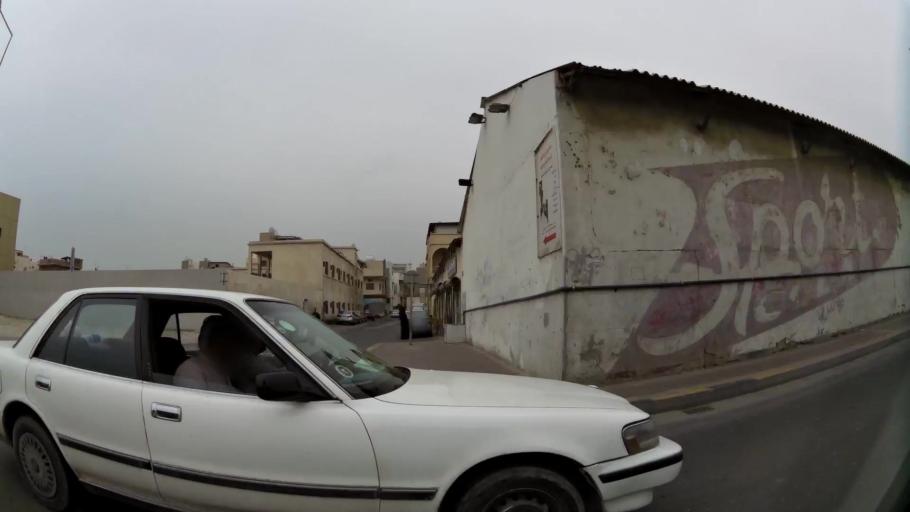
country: BH
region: Manama
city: Jidd Hafs
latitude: 26.2285
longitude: 50.5665
